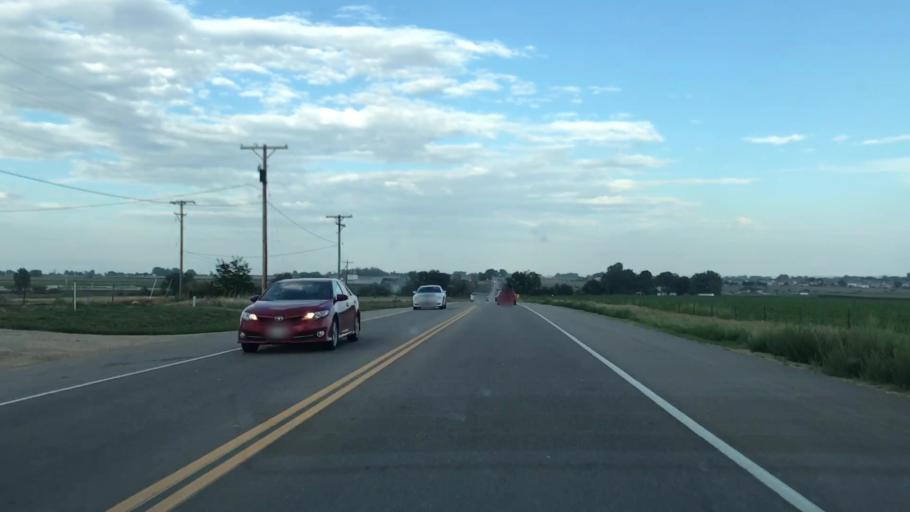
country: US
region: Colorado
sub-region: Weld County
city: Mead
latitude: 40.2038
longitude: -105.0251
